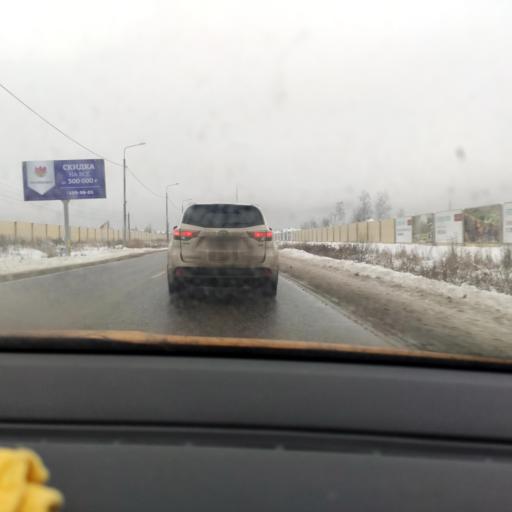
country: RU
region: Moskovskaya
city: Rozhdestveno
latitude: 55.8106
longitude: 36.9951
